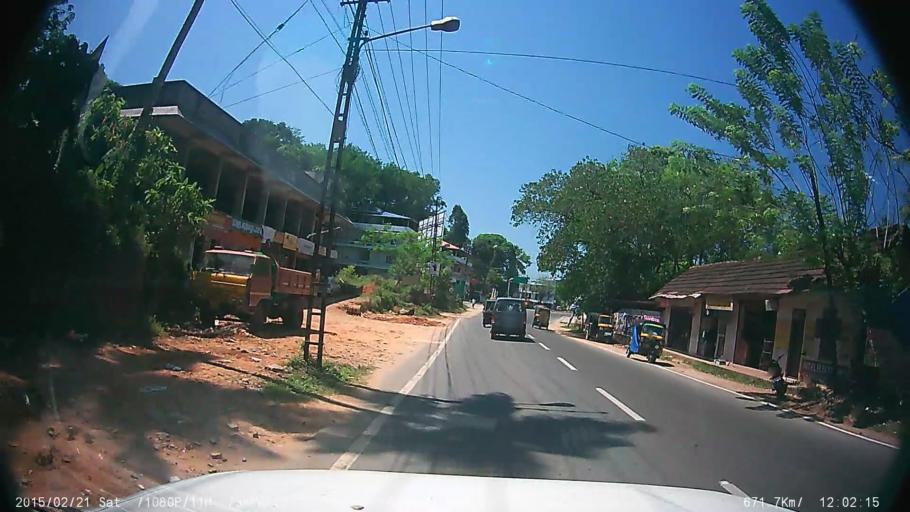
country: IN
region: Kerala
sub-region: Kottayam
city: Lalam
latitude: 9.7181
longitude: 76.6908
